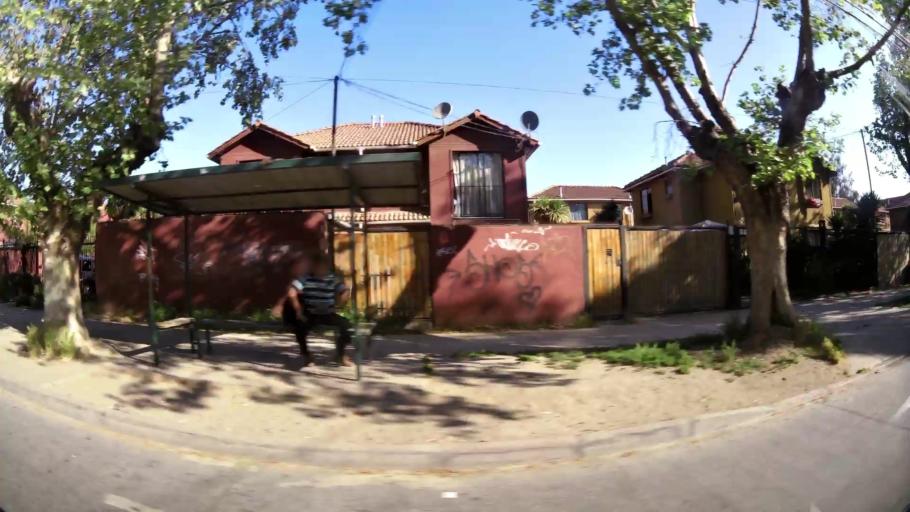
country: CL
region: Santiago Metropolitan
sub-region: Provincia de Talagante
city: Penaflor
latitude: -33.6101
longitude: -70.8625
